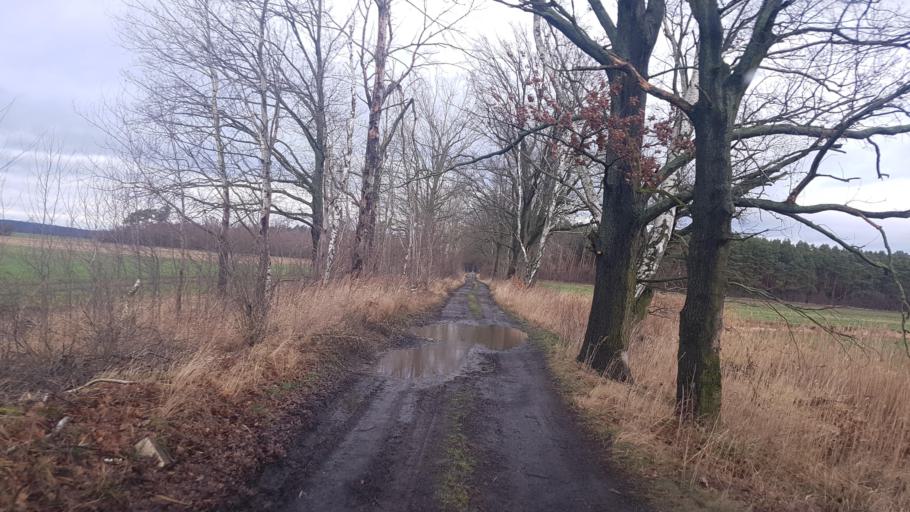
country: DE
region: Brandenburg
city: Plessa
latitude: 51.4332
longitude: 13.6500
